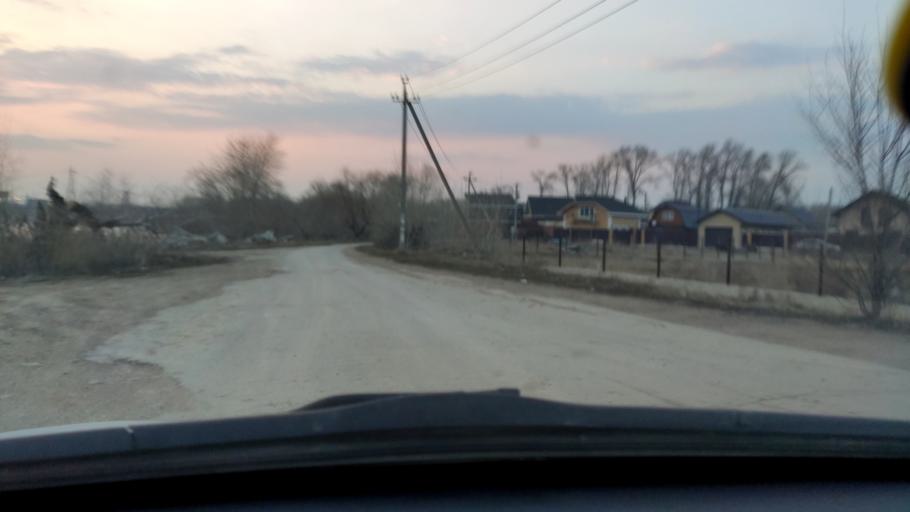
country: RU
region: Samara
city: Zhigulevsk
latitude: 53.4551
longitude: 49.5180
